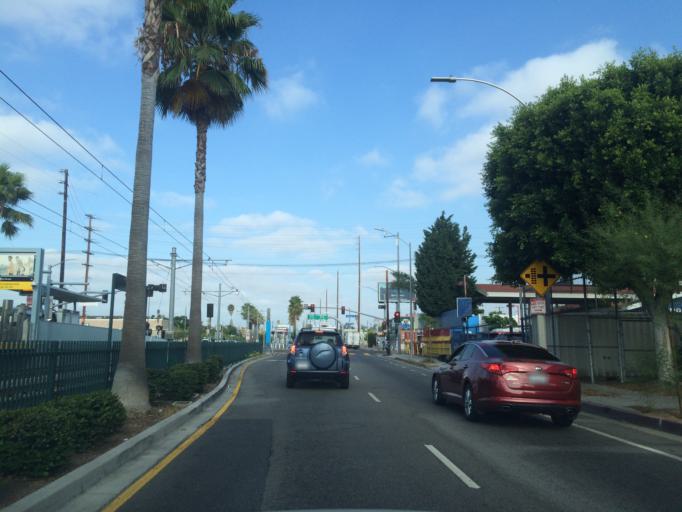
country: US
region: California
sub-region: Los Angeles County
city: View Park-Windsor Hills
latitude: 34.0184
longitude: -118.3080
